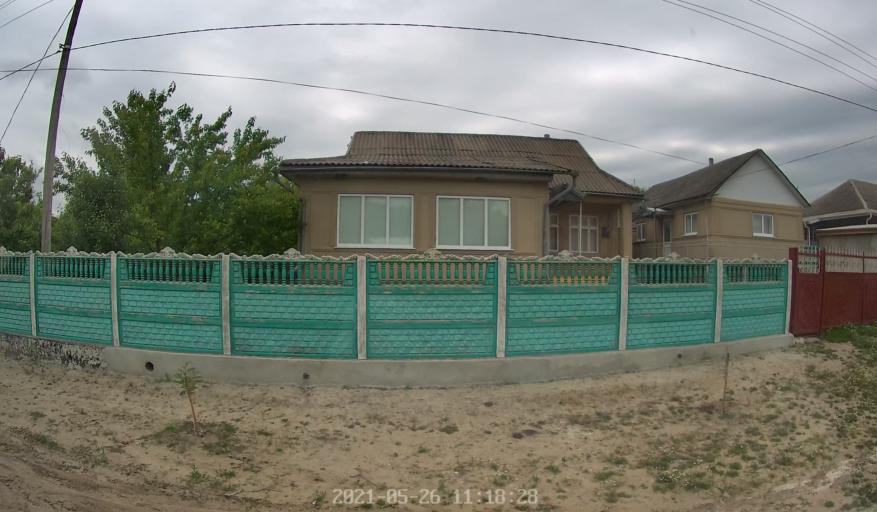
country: MD
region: Hincesti
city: Dancu
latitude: 46.8224
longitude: 28.3870
